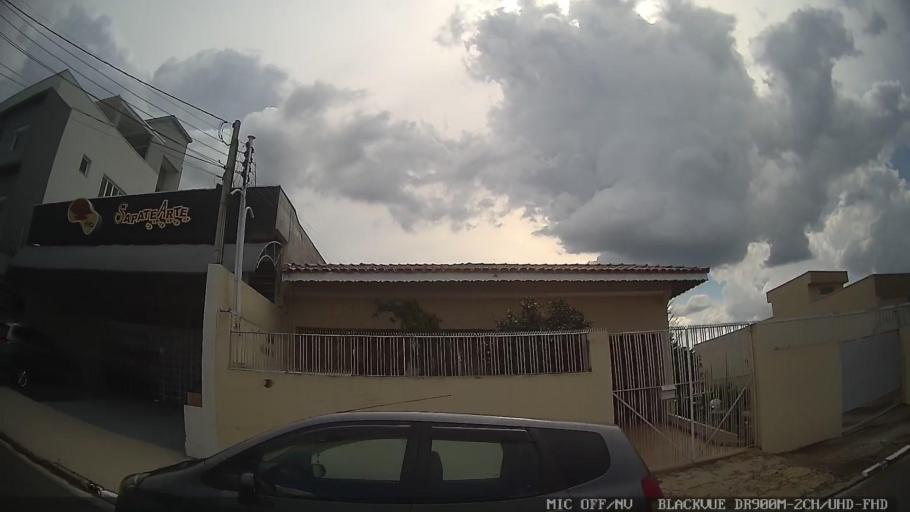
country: BR
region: Sao Paulo
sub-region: Atibaia
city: Atibaia
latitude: -23.1192
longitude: -46.5662
